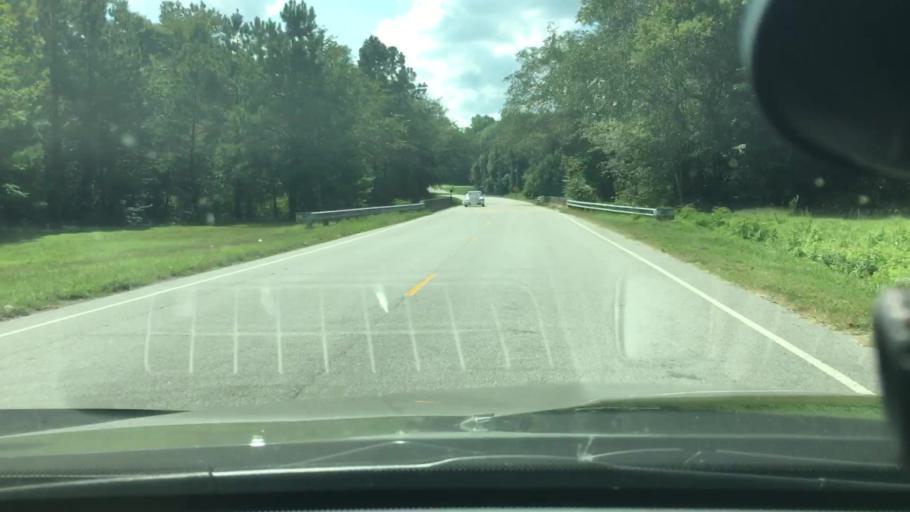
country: US
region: North Carolina
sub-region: Edgecombe County
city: Pinetops
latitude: 35.7231
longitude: -77.5305
